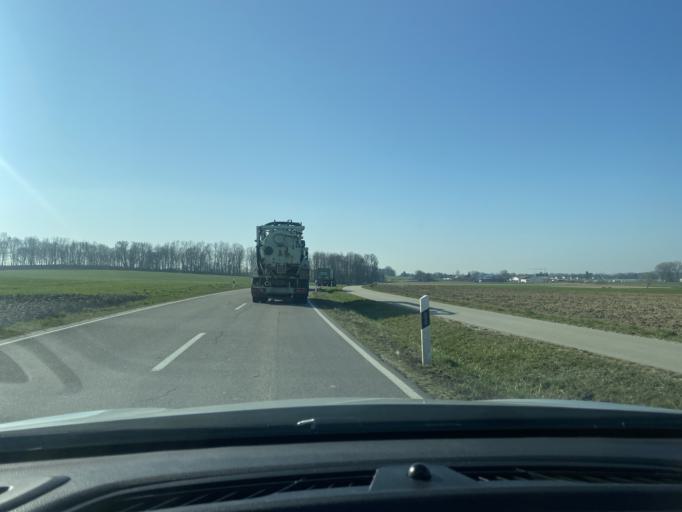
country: DE
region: Bavaria
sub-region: Upper Bavaria
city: Moosinning
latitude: 48.2924
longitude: 11.8492
